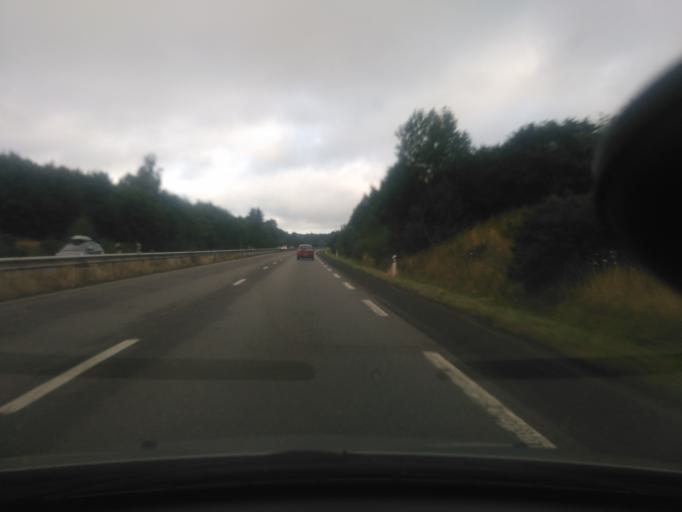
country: FR
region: Brittany
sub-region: Departement d'Ille-et-Vilaine
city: Hede-Bazouges
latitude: 48.2771
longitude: -1.7928
